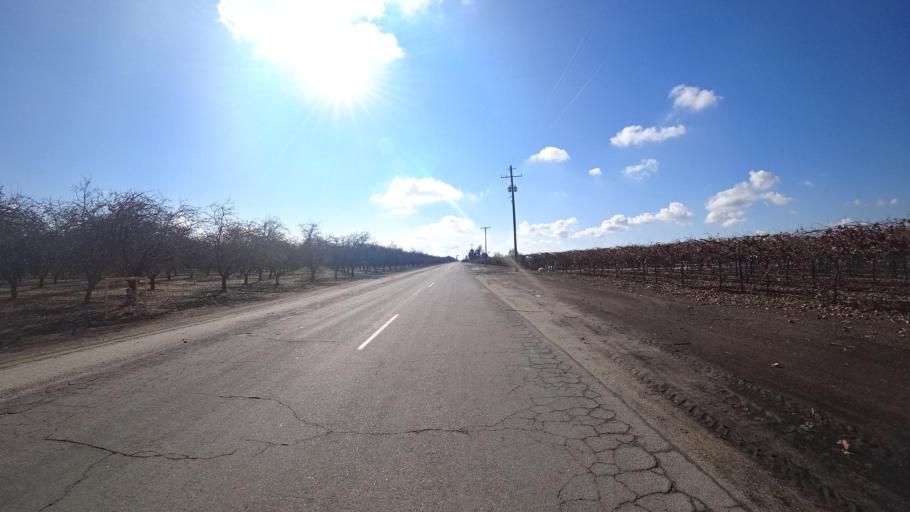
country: US
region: California
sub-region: Kern County
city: McFarland
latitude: 35.7073
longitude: -119.2586
